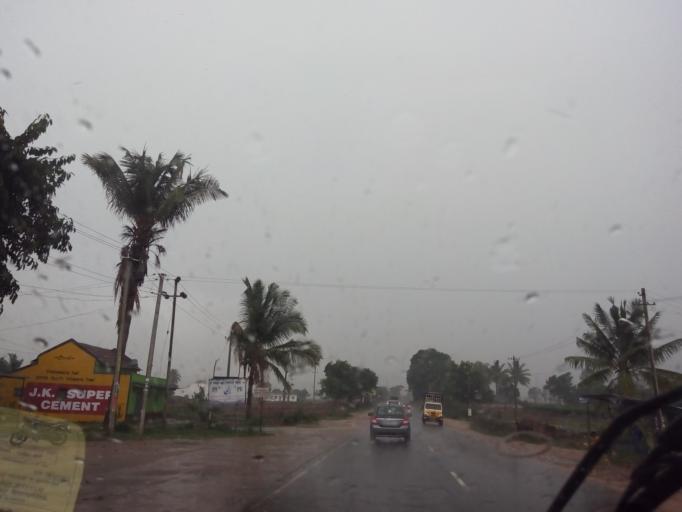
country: IN
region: Karnataka
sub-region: Hassan
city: Belur
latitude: 13.1193
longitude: 76.0009
